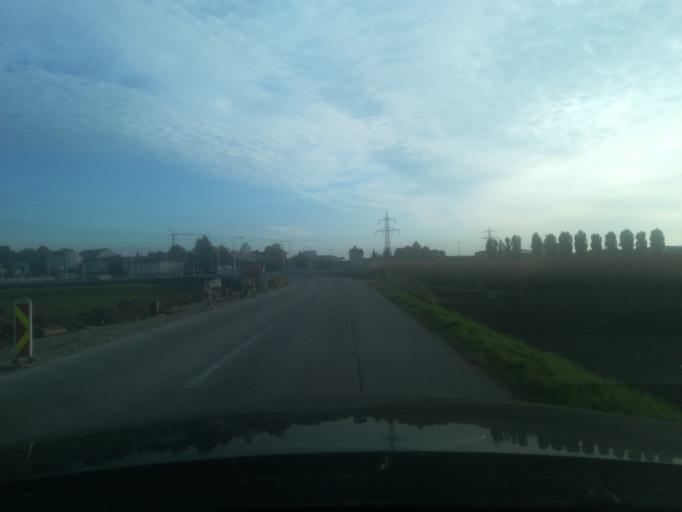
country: AT
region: Upper Austria
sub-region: Wels-Land
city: Gunskirchen
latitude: 48.1358
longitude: 13.9393
